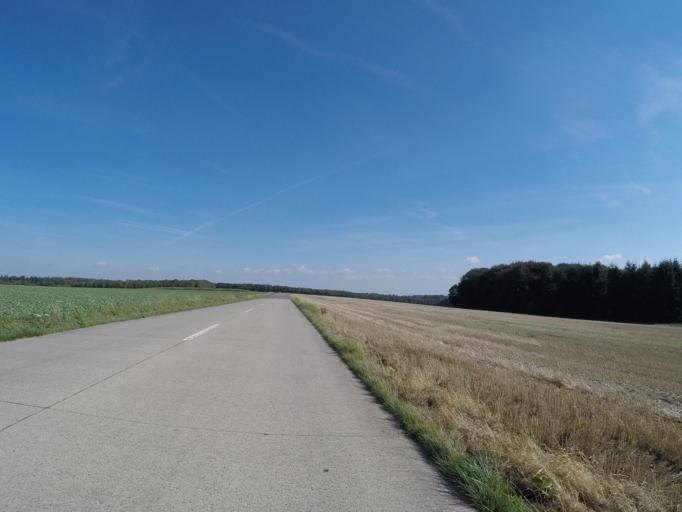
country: BE
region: Wallonia
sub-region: Province de Namur
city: Assesse
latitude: 50.3394
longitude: 5.0017
